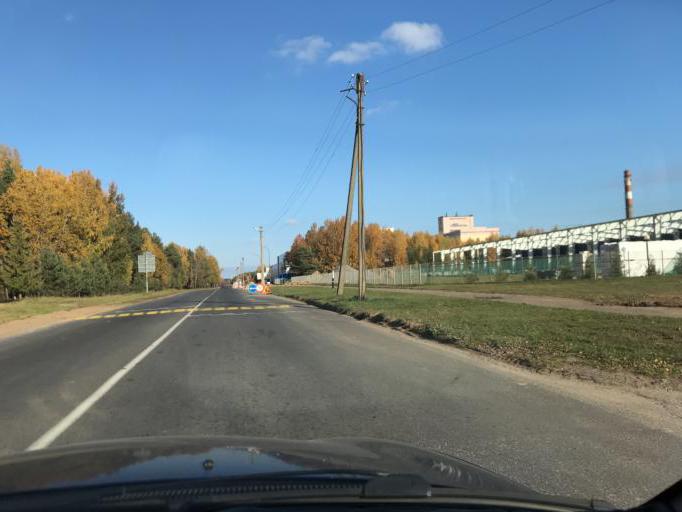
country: BY
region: Grodnenskaya
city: Lida
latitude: 53.9355
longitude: 25.2448
